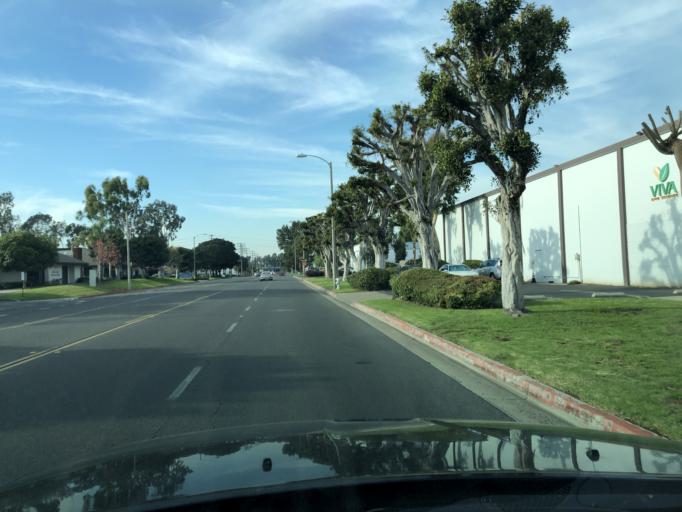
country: US
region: California
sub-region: Orange County
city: Irvine
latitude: 33.6786
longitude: -117.8721
